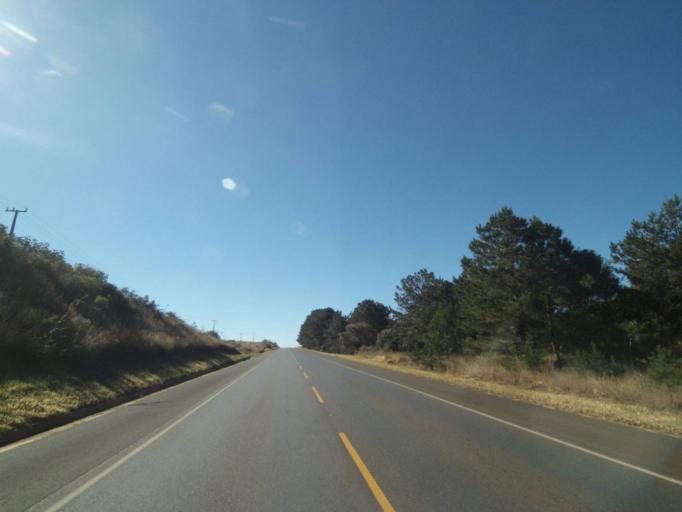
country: BR
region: Parana
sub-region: Tibagi
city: Tibagi
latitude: -24.3668
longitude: -50.3245
